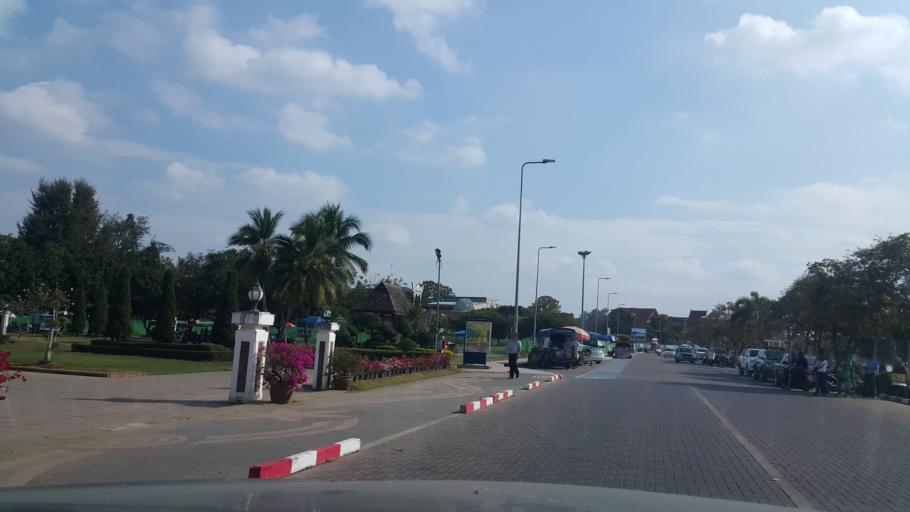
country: TH
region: Phayao
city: Phayao
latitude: 19.1687
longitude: 99.8955
